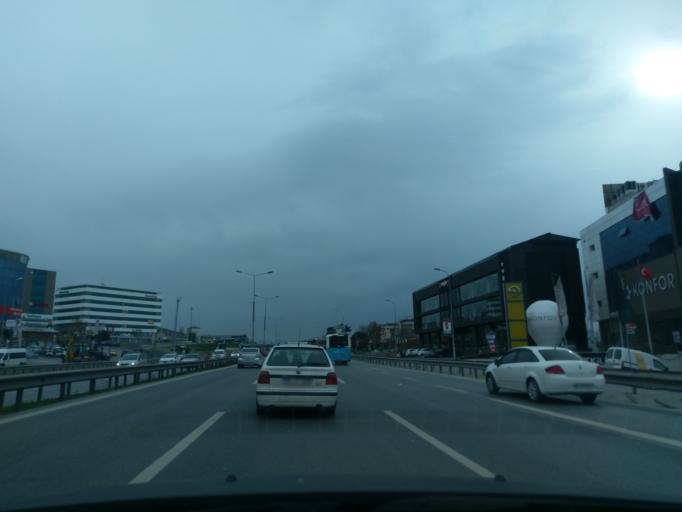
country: TR
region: Istanbul
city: Pendik
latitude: 40.8904
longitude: 29.2353
